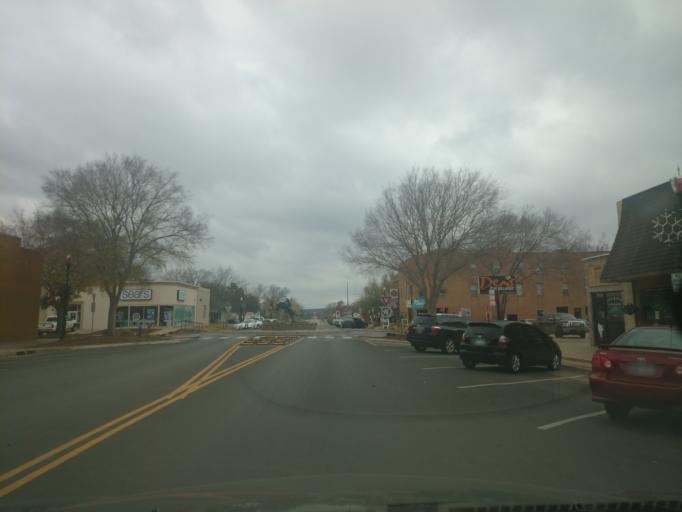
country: US
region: Oklahoma
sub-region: Payne County
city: Stillwater
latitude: 36.1118
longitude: -97.0586
